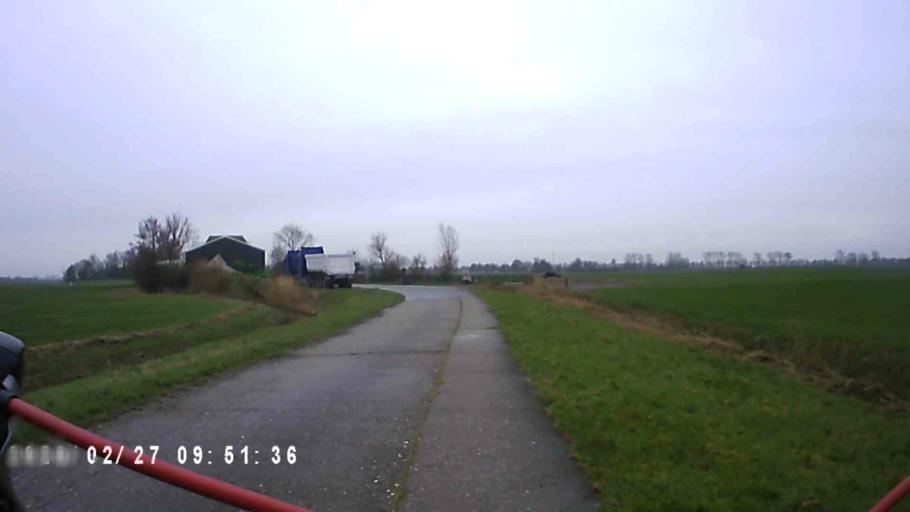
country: NL
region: Groningen
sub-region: Gemeente Zuidhorn
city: Aduard
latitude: 53.2694
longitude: 6.4585
